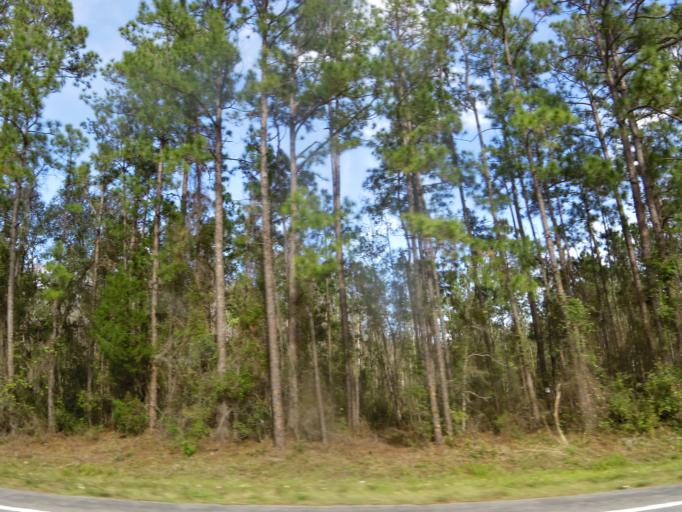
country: US
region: Florida
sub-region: Volusia County
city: Pierson
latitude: 29.2573
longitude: -81.3296
